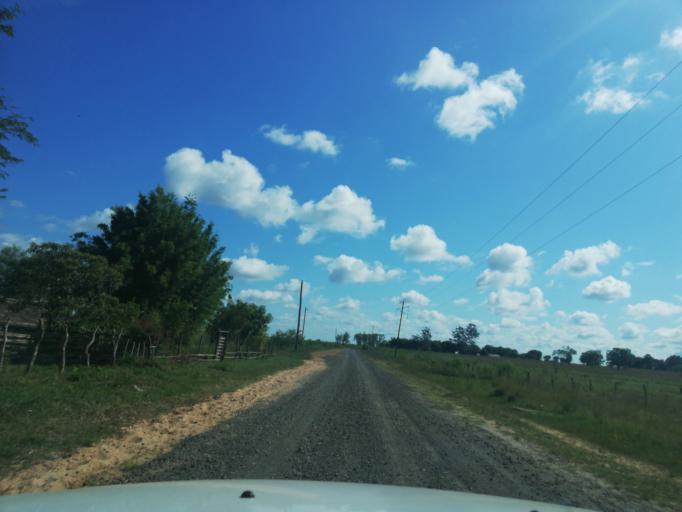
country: AR
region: Corrientes
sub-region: Departamento de San Miguel
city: San Miguel
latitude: -27.9845
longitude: -57.5830
